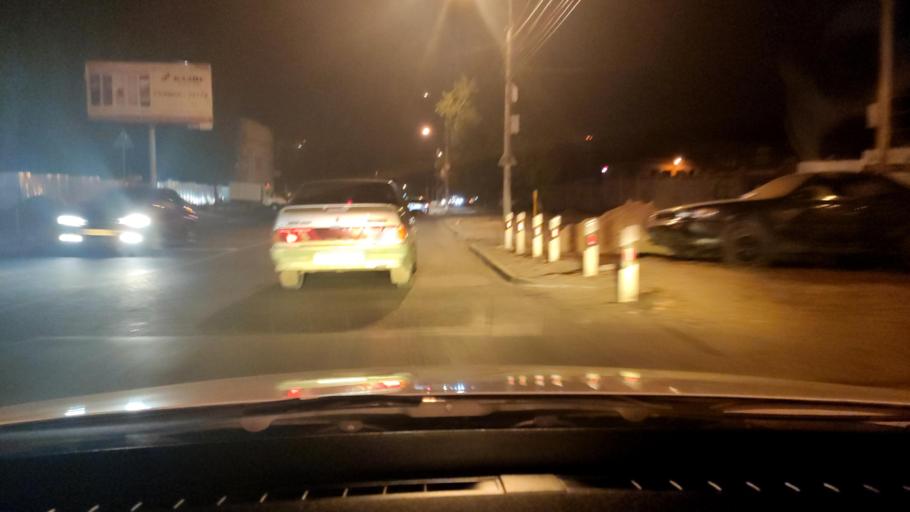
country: RU
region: Voronezj
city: Voronezh
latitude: 51.6654
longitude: 39.1506
